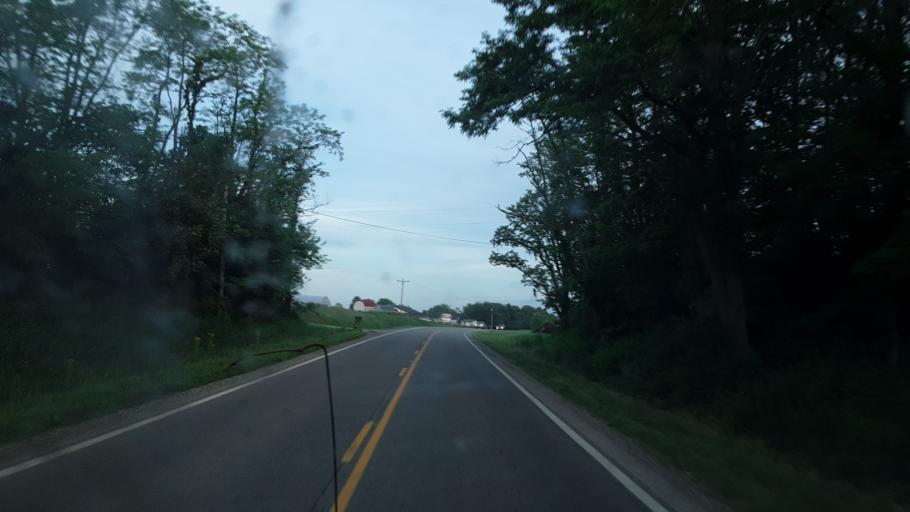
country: US
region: Ohio
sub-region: Ross County
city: Kingston
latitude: 39.4527
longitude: -82.7808
